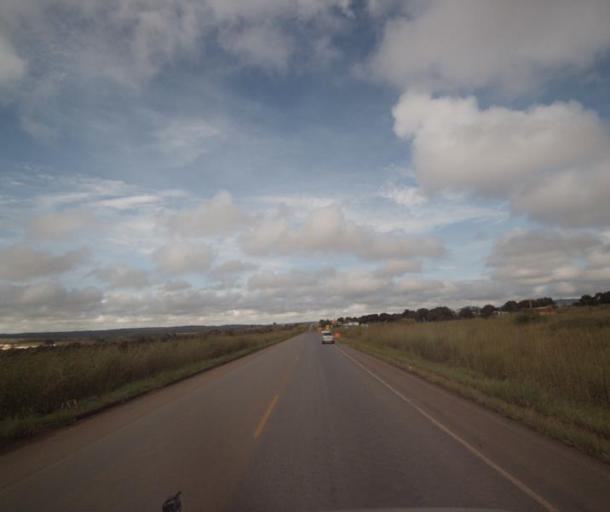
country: BR
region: Goias
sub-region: Pirenopolis
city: Pirenopolis
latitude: -15.7683
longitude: -48.7602
